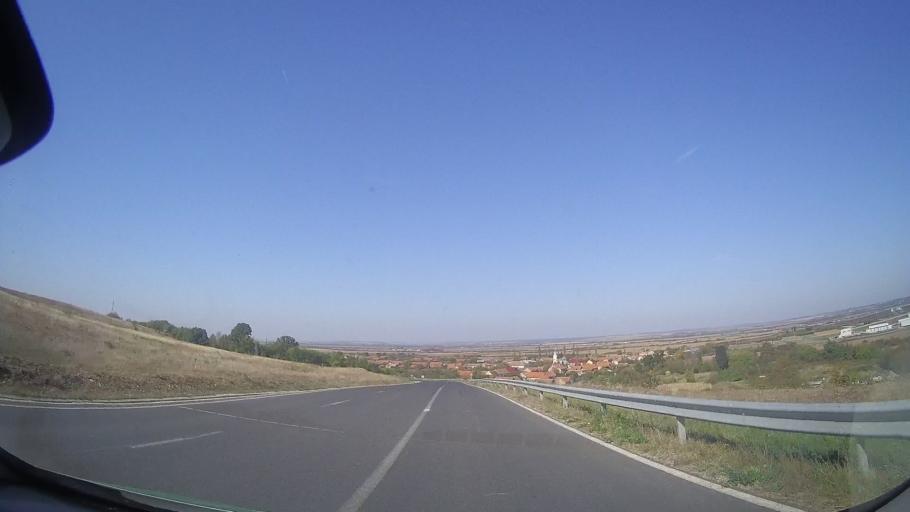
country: RO
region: Timis
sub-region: Comuna Costeiu
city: Costeiu
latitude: 45.7729
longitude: 21.8532
